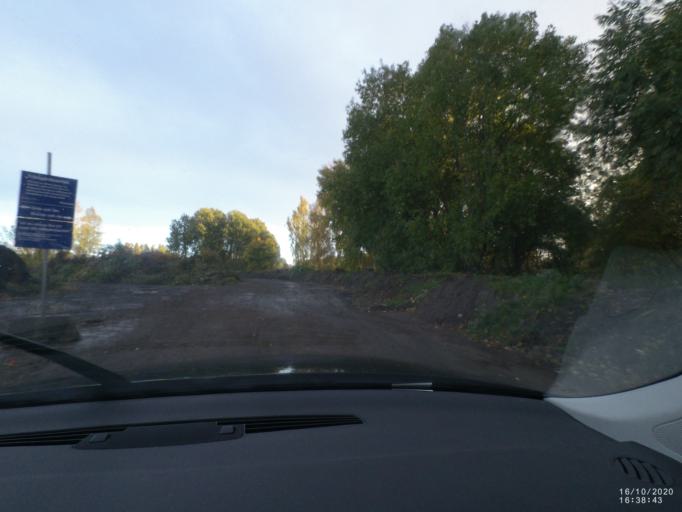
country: SE
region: Soedermanland
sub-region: Nykopings Kommun
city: Nykoping
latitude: 58.7476
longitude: 17.0495
